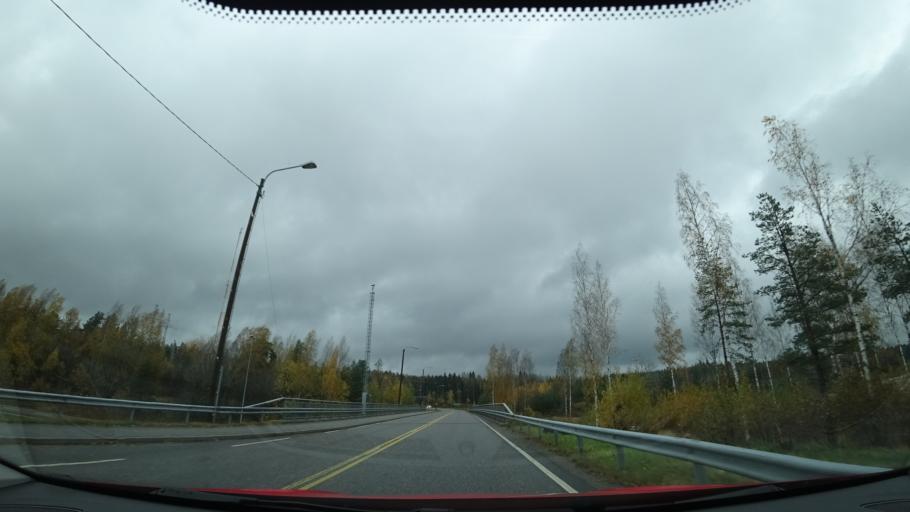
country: FI
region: Uusimaa
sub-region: Helsinki
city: Sibbo
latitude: 60.2659
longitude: 25.2098
